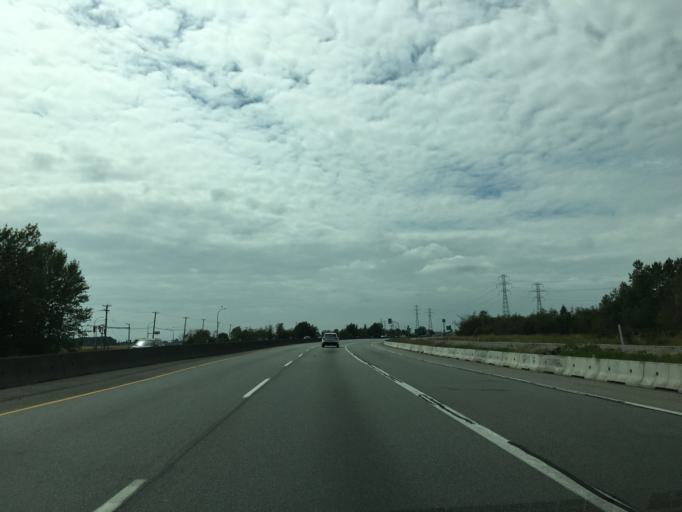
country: CA
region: British Columbia
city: Ladner
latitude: 49.0905
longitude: -122.9996
